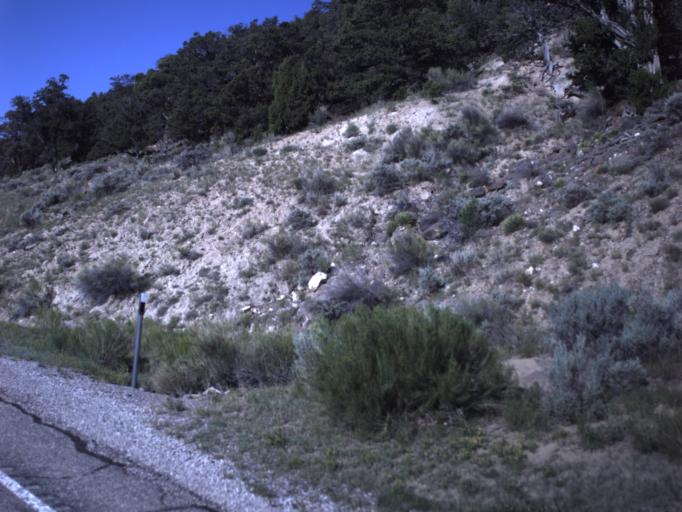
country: US
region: Utah
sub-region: Wayne County
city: Loa
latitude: 38.6632
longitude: -111.4285
